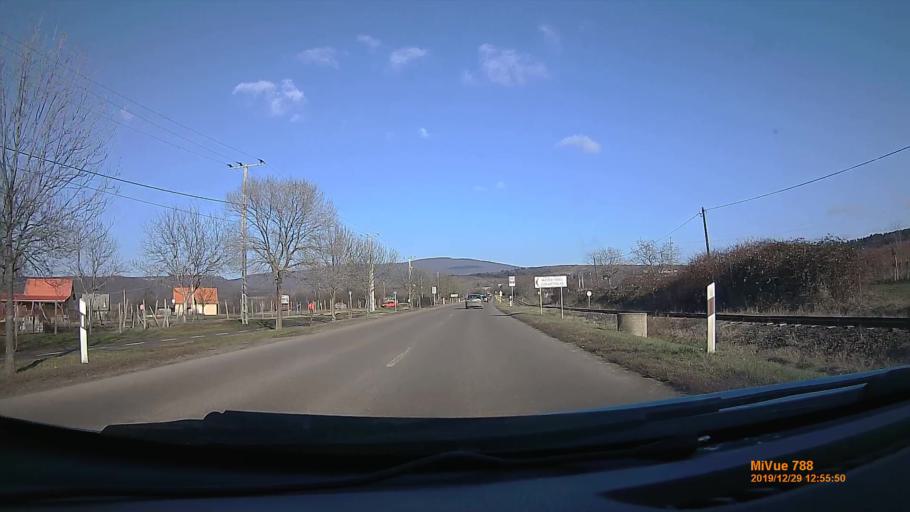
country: HU
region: Heves
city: Gyongyossolymos
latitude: 47.8072
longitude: 19.9524
